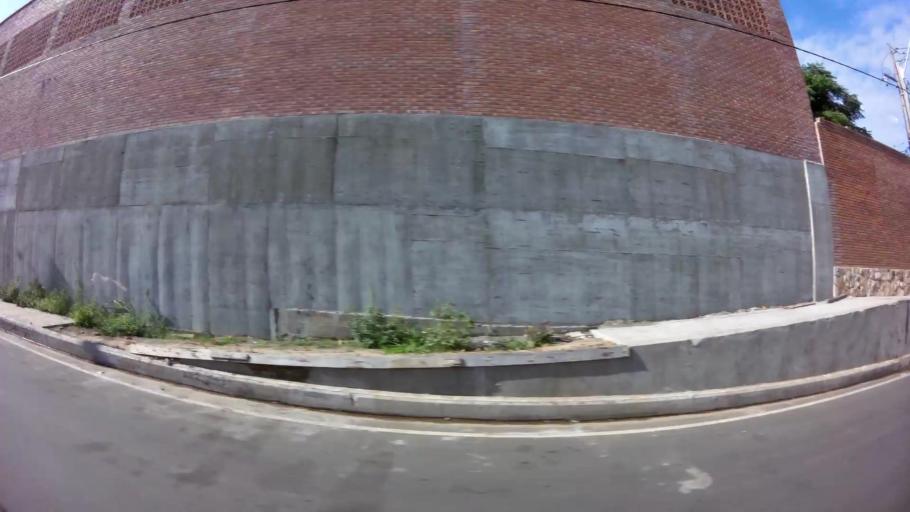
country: PY
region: Asuncion
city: Asuncion
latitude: -25.2566
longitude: -57.5599
